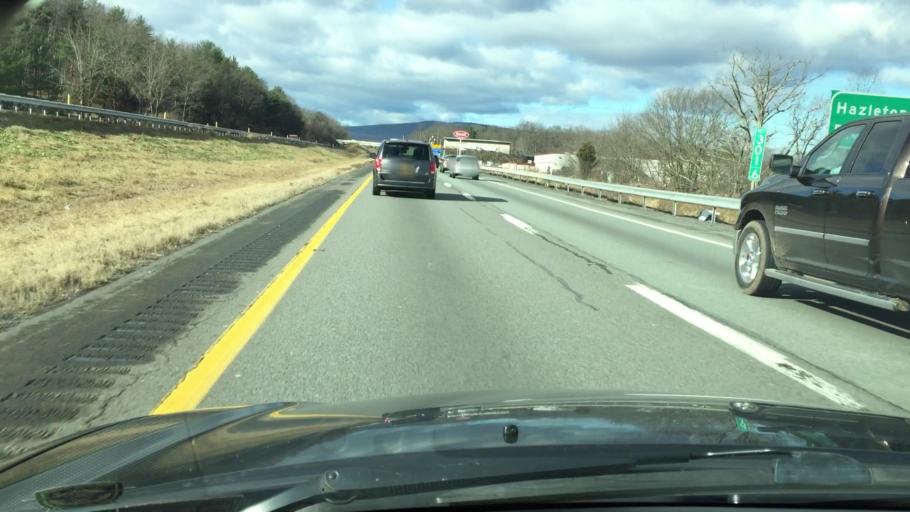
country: US
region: Pennsylvania
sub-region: Monroe County
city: Tannersville
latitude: 41.0049
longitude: -75.2837
